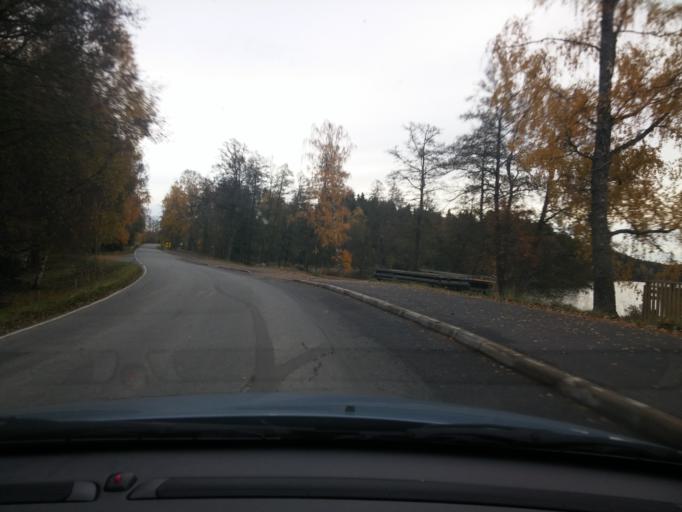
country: FI
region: Haeme
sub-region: Forssa
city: Tammela
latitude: 60.7925
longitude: 23.8154
